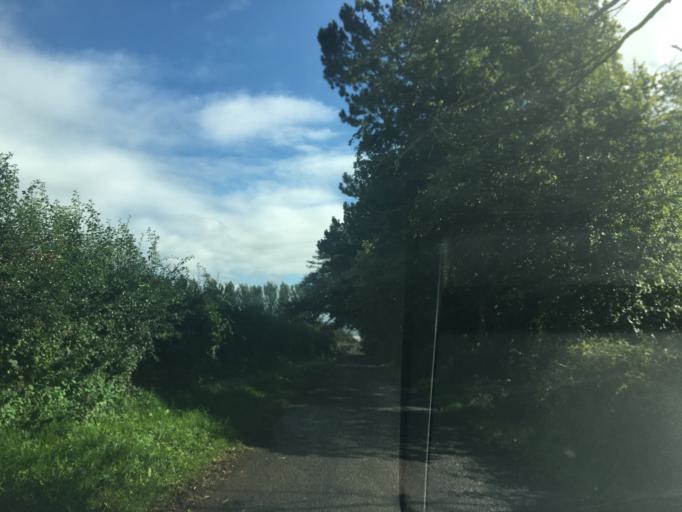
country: GB
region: Scotland
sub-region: Edinburgh
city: Kirkliston
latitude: 55.9551
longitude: -3.3725
